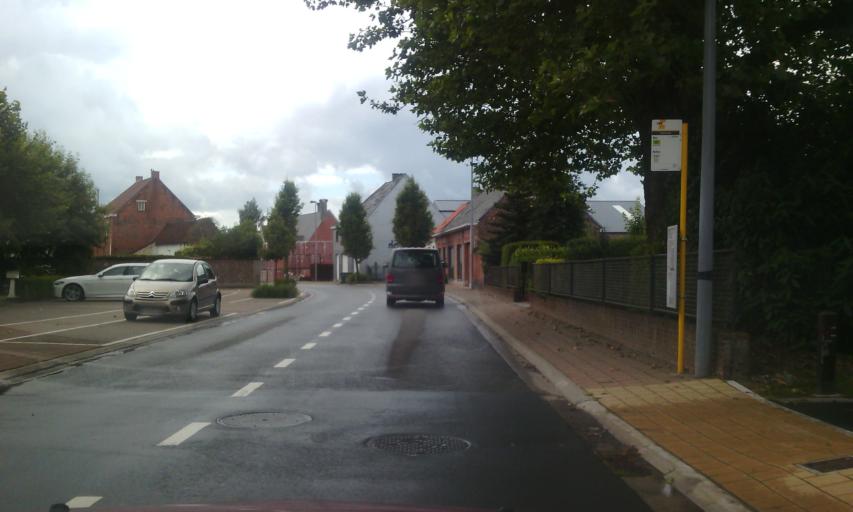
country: BE
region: Flanders
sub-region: Provincie Oost-Vlaanderen
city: Wetteren
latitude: 51.0342
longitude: 3.9128
